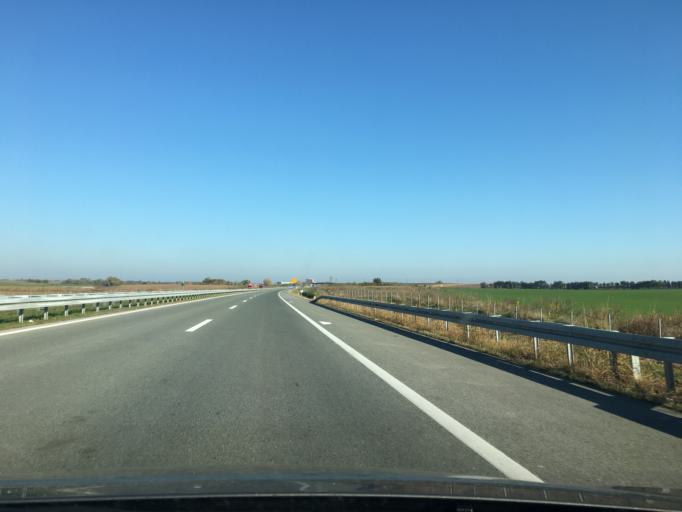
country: RS
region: Autonomna Pokrajina Vojvodina
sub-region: Severnobacki Okrug
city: Mali Igos
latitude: 45.6326
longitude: 19.7087
